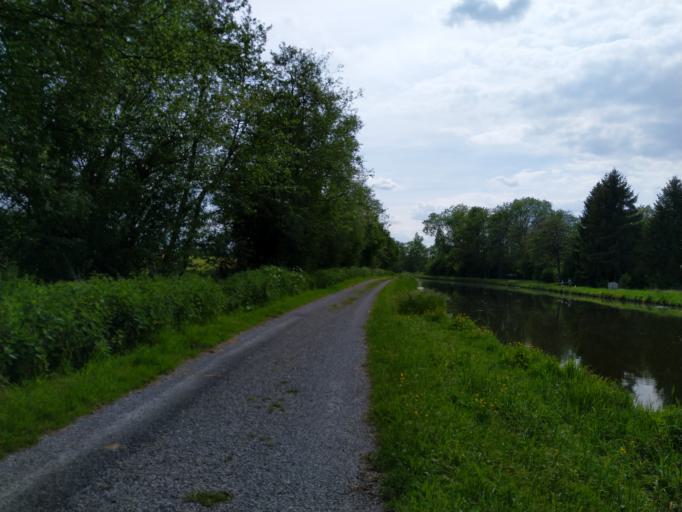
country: FR
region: Picardie
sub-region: Departement de l'Aisne
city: Etreux
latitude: 49.9787
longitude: 3.6357
